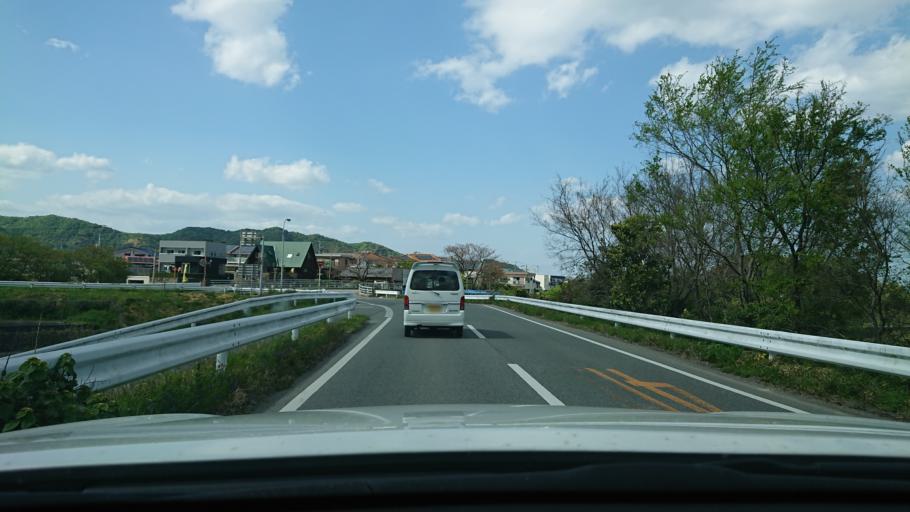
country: JP
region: Tokushima
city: Komatsushimacho
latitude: 33.9998
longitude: 134.5474
